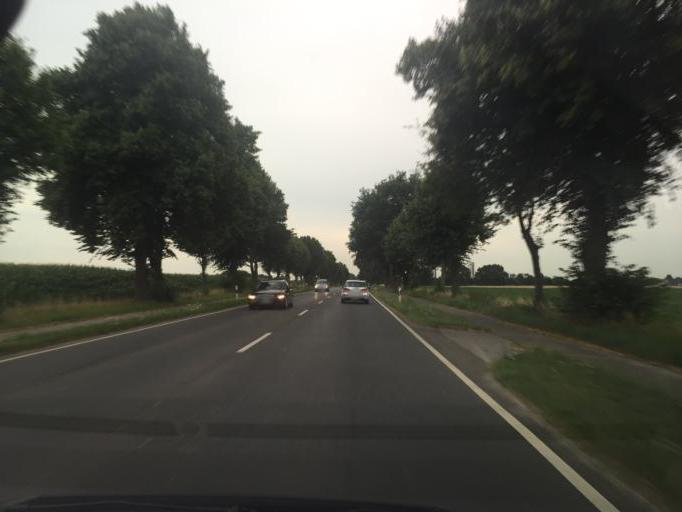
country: DE
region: North Rhine-Westphalia
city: Wegberg
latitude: 51.1326
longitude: 6.3377
